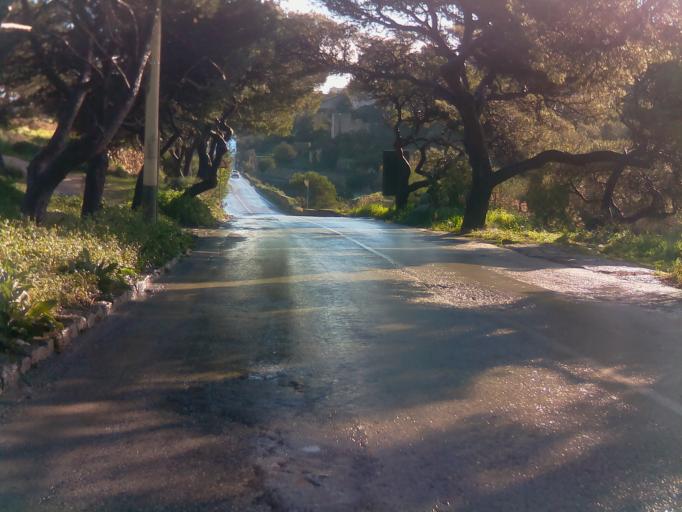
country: MT
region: Il-Mellieha
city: Mellieha
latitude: 35.9532
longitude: 14.3792
